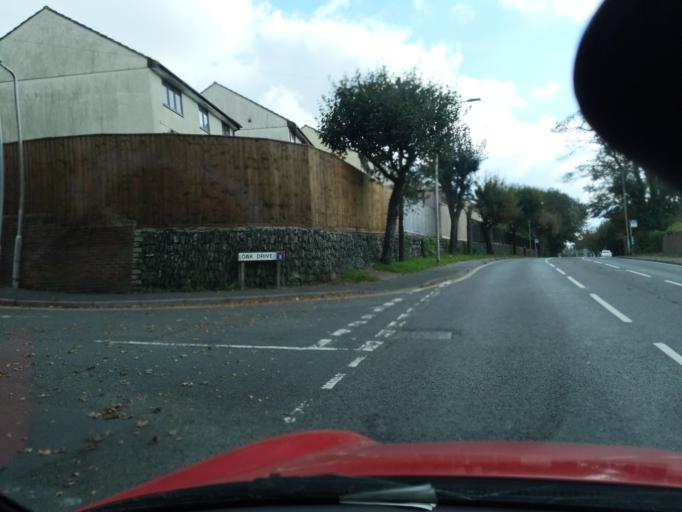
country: GB
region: England
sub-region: Plymouth
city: Plymouth
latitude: 50.4138
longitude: -4.1346
